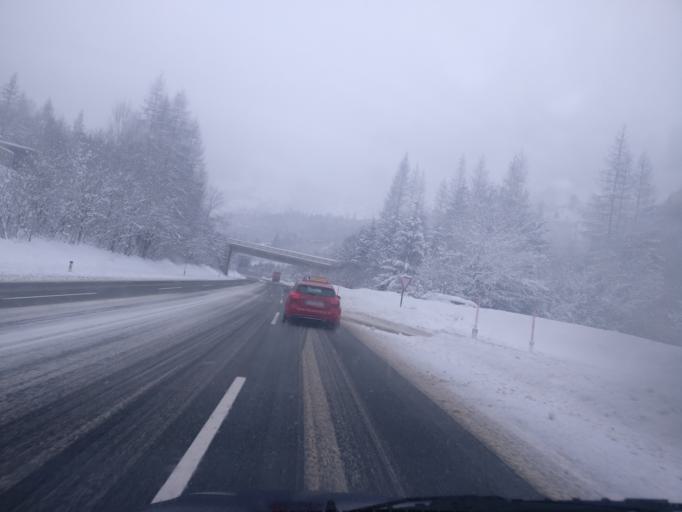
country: AT
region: Salzburg
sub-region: Politischer Bezirk Zell am See
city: Lend
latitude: 47.3056
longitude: 13.0274
